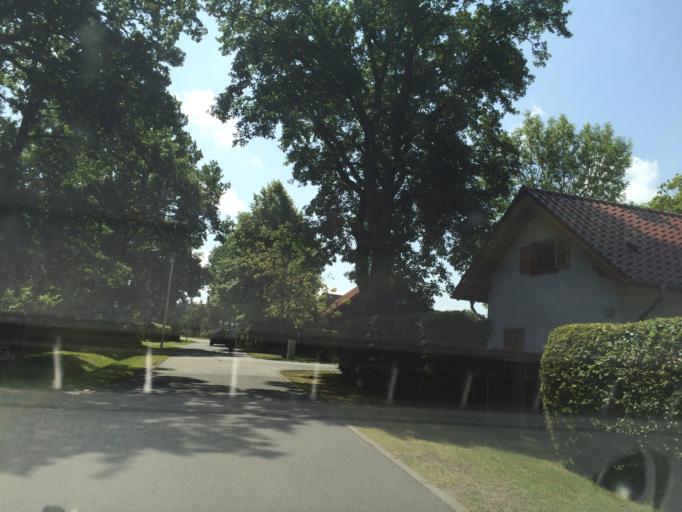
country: DE
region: Mecklenburg-Vorpommern
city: Zingst
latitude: 54.4325
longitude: 12.6801
